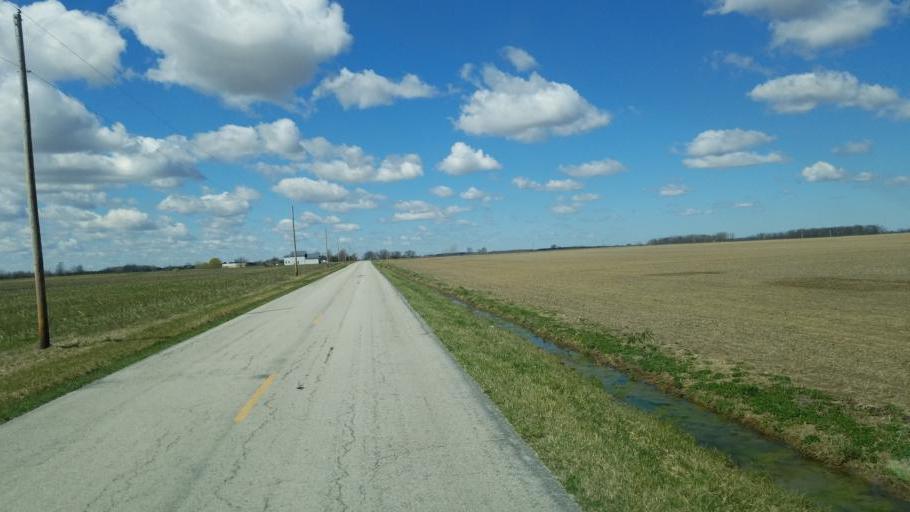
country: US
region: Ohio
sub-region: Sandusky County
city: Mount Carmel
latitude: 41.2418
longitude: -82.9905
